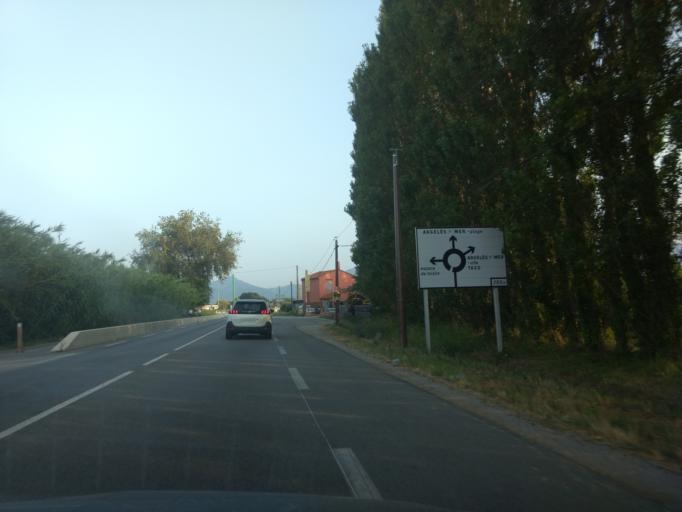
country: FR
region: Languedoc-Roussillon
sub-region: Departement des Pyrenees-Orientales
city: Argelers
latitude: 42.5781
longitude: 3.0333
